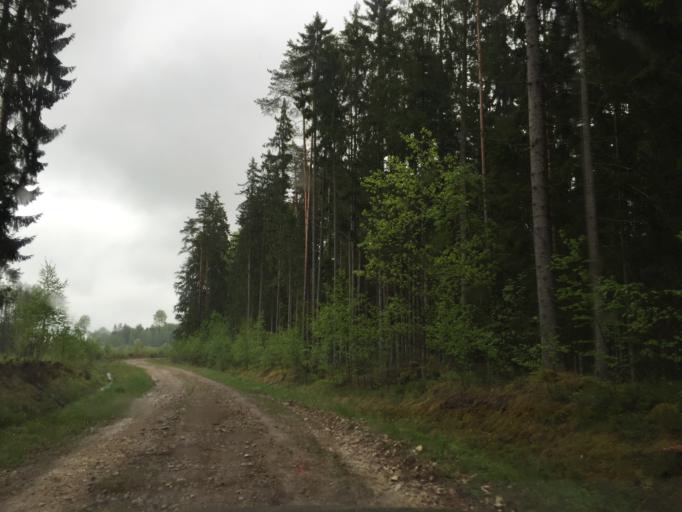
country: LV
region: Ogre
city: Jumprava
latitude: 56.6775
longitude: 24.9275
